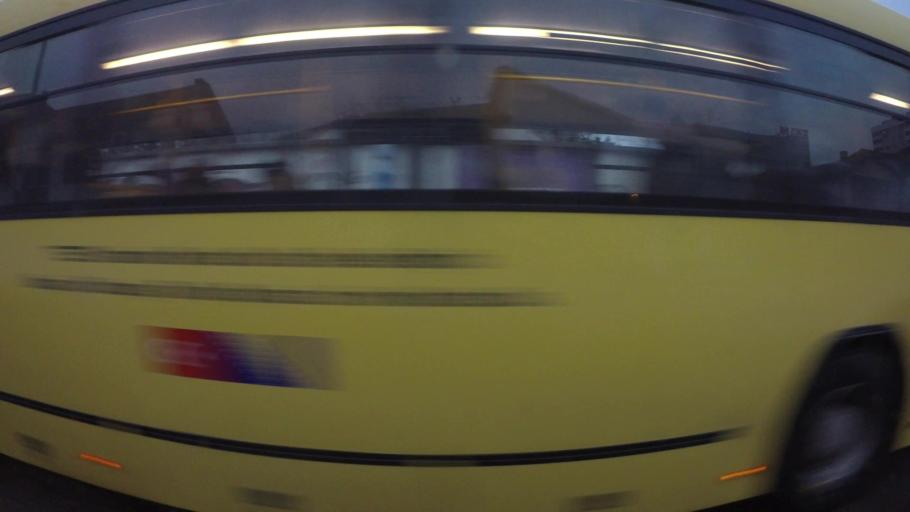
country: BA
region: Federation of Bosnia and Herzegovina
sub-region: Hercegovacko-Bosanski Kanton
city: Mostar
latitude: 43.3548
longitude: 17.8124
